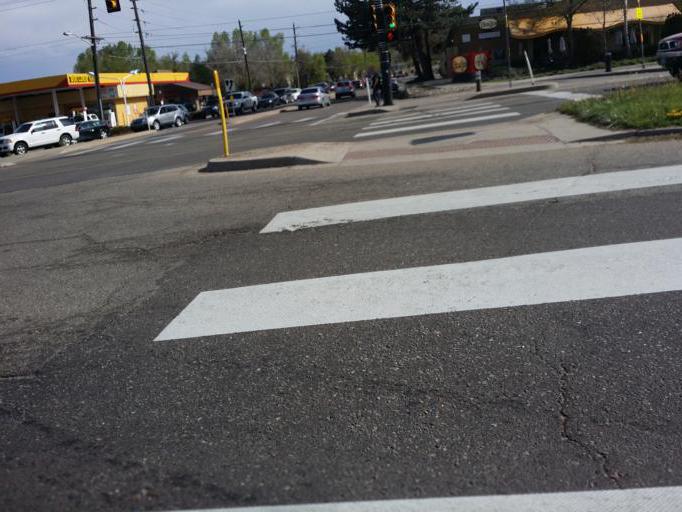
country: US
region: Colorado
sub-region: Boulder County
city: Boulder
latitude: 40.0005
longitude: -105.2603
